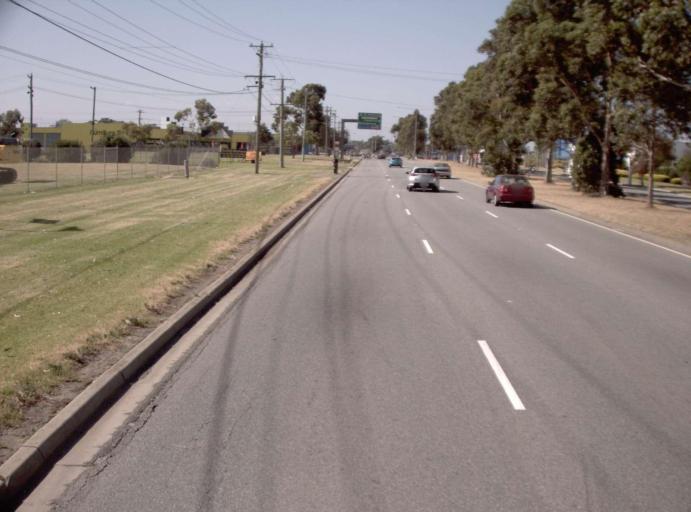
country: AU
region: Victoria
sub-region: Casey
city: Doveton
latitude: -38.0082
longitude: 145.2165
